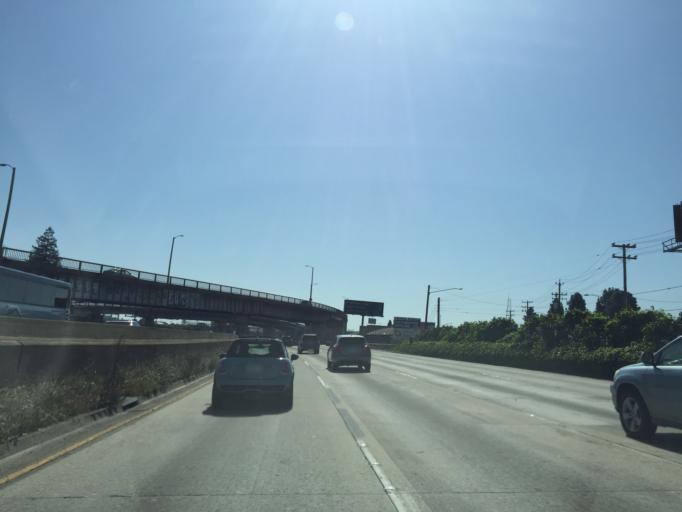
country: US
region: California
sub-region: Alameda County
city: Alameda
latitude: 37.7789
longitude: -122.2379
